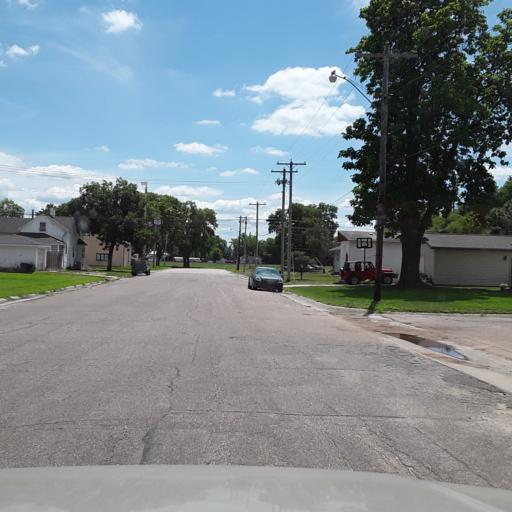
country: US
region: Nebraska
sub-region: Platte County
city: Columbus
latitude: 41.3906
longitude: -97.4947
